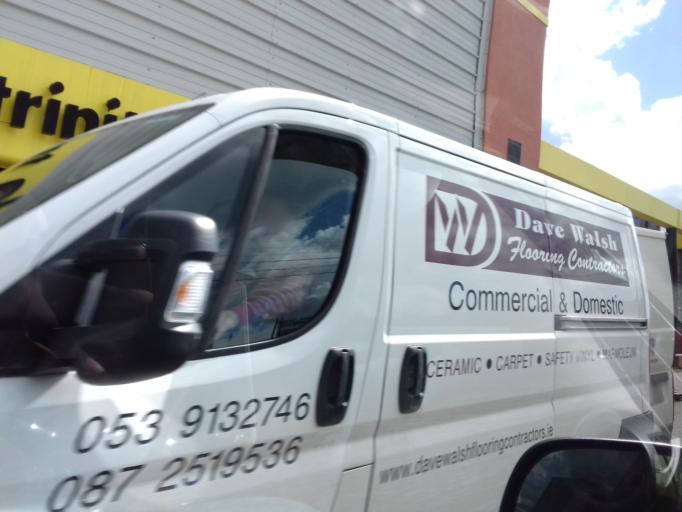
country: IE
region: Leinster
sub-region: Loch Garman
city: Loch Garman
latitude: 52.3351
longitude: -6.4563
